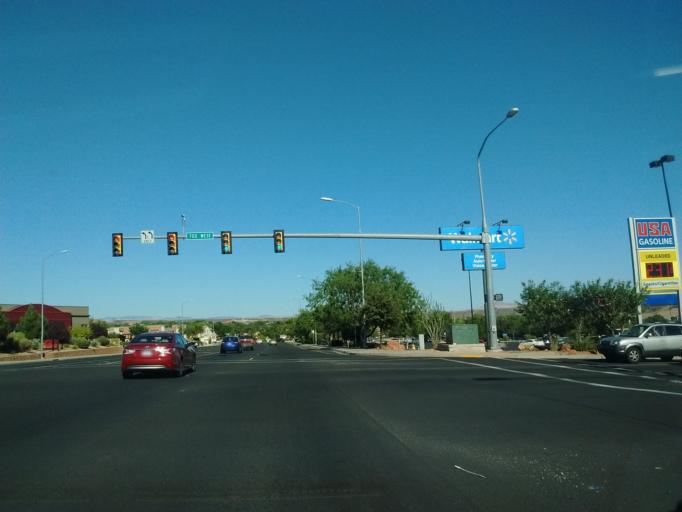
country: US
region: Utah
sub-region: Washington County
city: Washington
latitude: 37.1281
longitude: -113.5207
